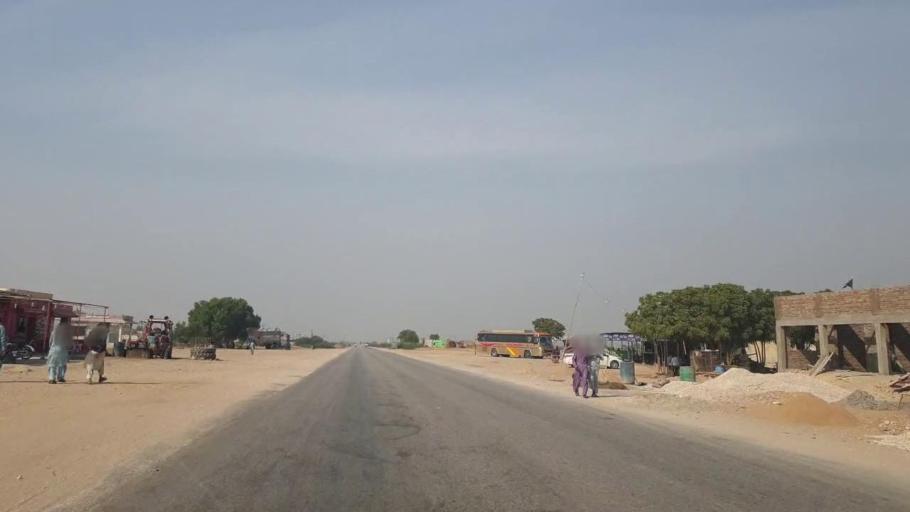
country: PK
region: Sindh
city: Sann
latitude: 26.0580
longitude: 68.1049
